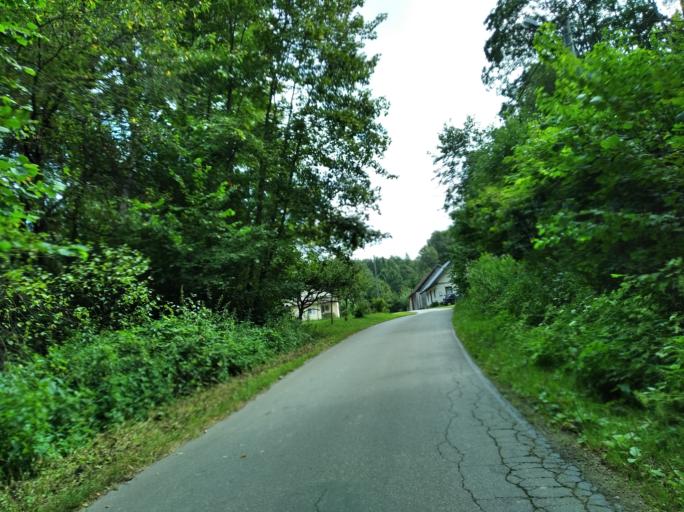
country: PL
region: Subcarpathian Voivodeship
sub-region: Powiat krosnienski
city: Wojaszowka
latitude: 49.7856
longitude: 21.6996
